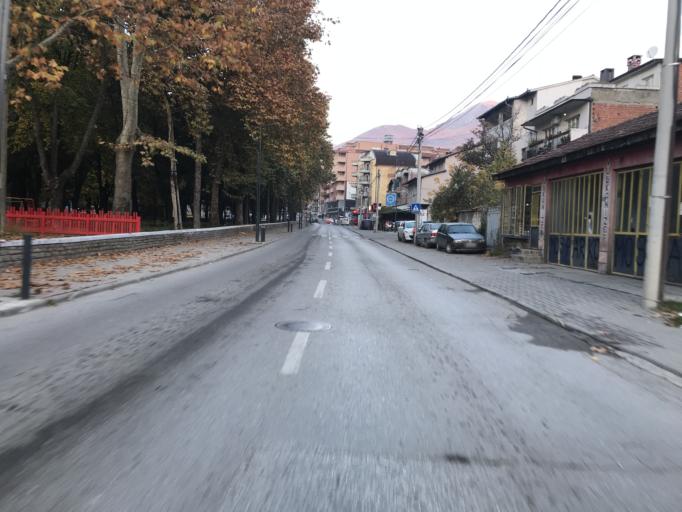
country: XK
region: Pec
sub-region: Komuna e Pejes
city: Peje
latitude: 42.6617
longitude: 20.2909
